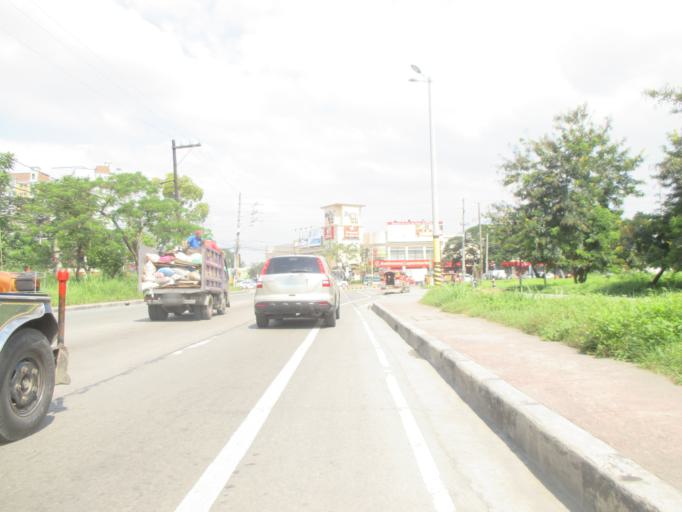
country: PH
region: Metro Manila
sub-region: Marikina
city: Calumpang
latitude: 14.6340
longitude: 121.1019
